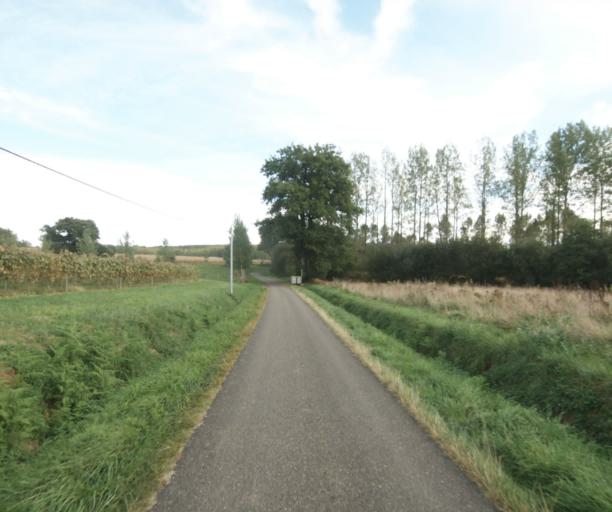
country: FR
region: Midi-Pyrenees
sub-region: Departement du Gers
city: Cazaubon
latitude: 43.8664
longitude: -0.1211
